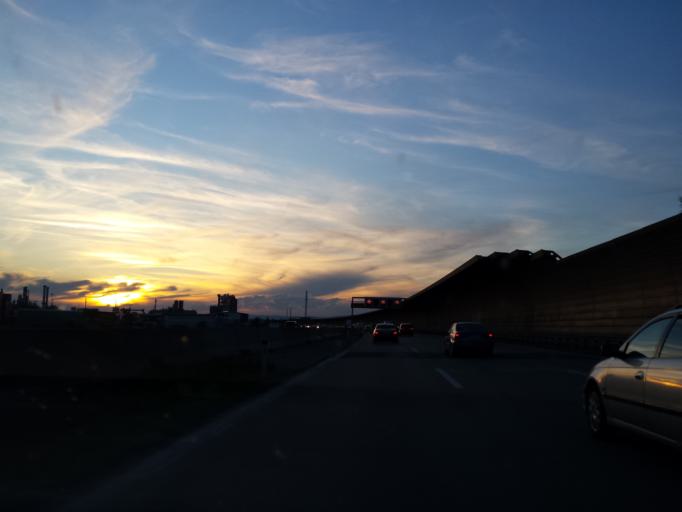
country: AT
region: Lower Austria
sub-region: Politischer Bezirk Wien-Umgebung
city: Rauchenwarth
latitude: 48.1394
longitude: 16.5238
